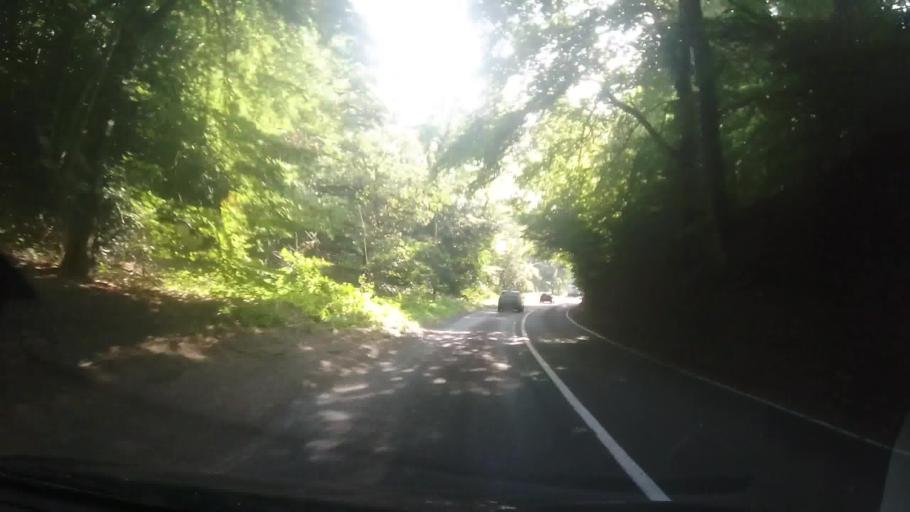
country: GB
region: England
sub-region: Shropshire
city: Alveley
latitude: 52.5015
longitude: -2.3770
